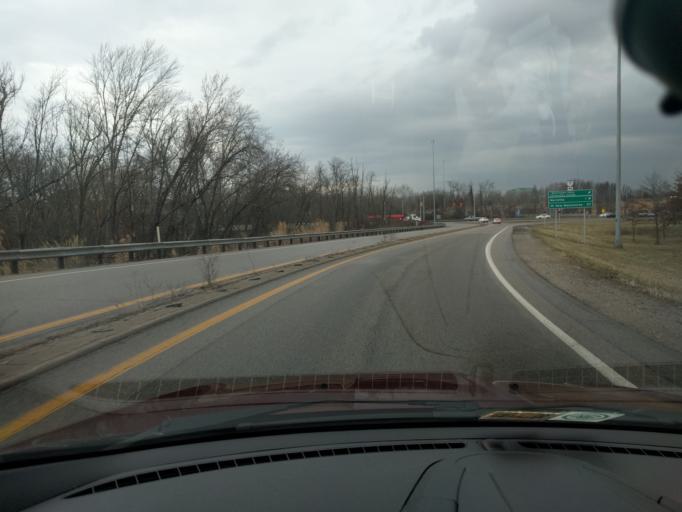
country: US
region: West Virginia
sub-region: Wood County
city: Williamstown
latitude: 39.4102
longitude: -81.4224
